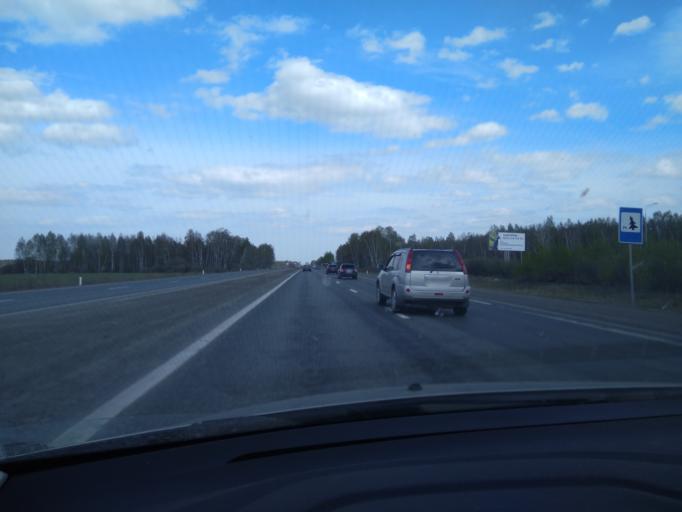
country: RU
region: Tjumen
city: Moskovskiy
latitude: 57.1022
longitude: 65.3211
